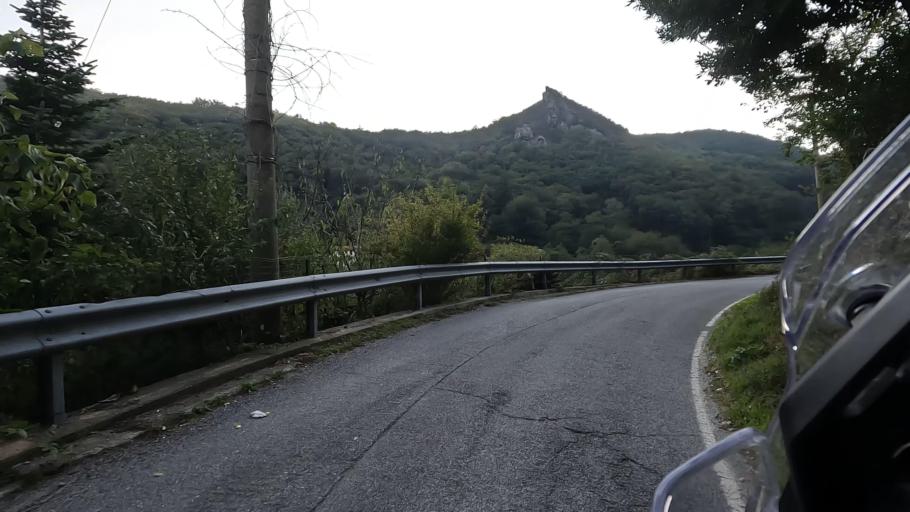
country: IT
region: Liguria
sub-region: Provincia di Savona
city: San Giovanni
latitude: 44.4032
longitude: 8.5306
